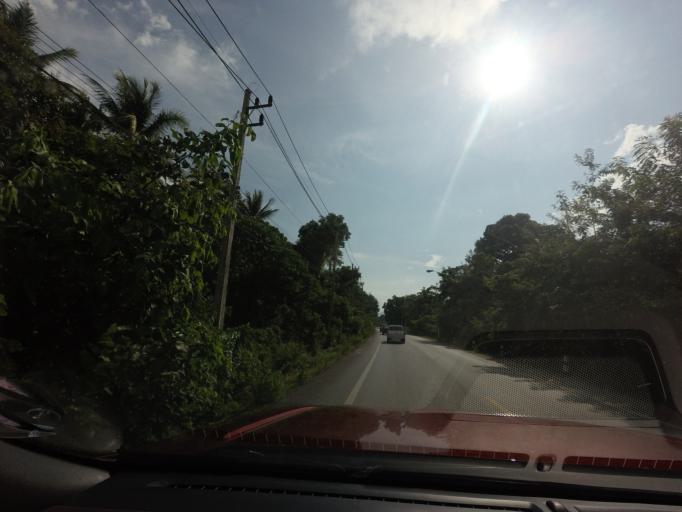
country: TH
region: Yala
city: Yala
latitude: 6.5478
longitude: 101.2462
